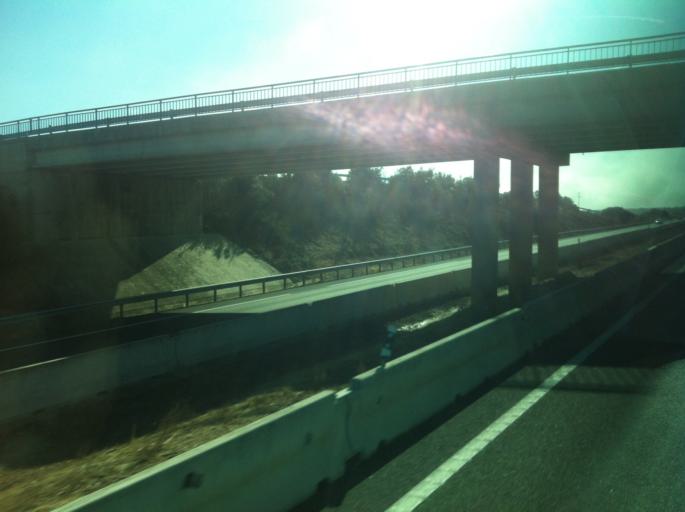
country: ES
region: Castille and Leon
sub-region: Provincia de Burgos
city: Madrigalejo del Monte
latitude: 42.0929
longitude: -3.7268
